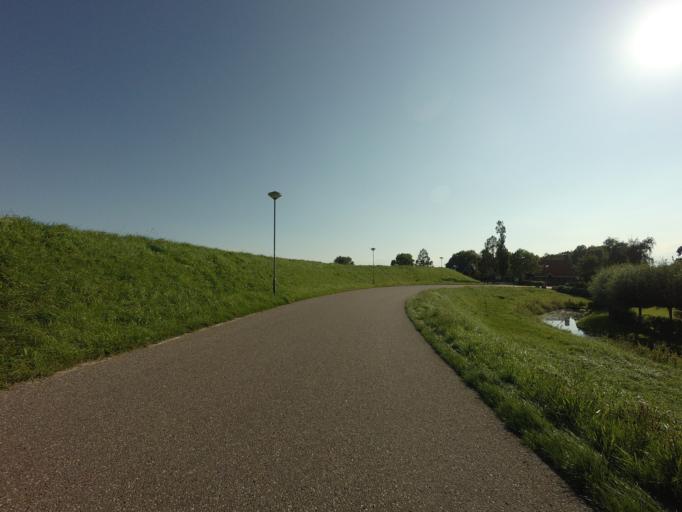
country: NL
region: North Holland
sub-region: Gemeente Enkhuizen
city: Enkhuizen
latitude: 52.6789
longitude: 5.2433
